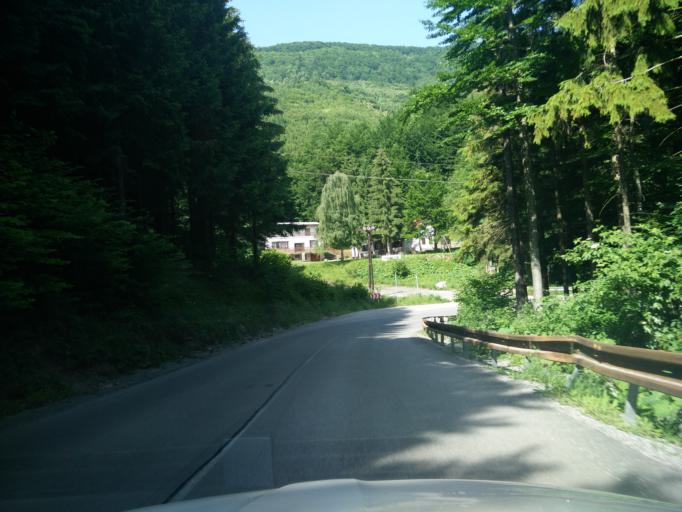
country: SK
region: Zilinsky
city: Rajec
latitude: 48.9548
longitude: 18.6232
